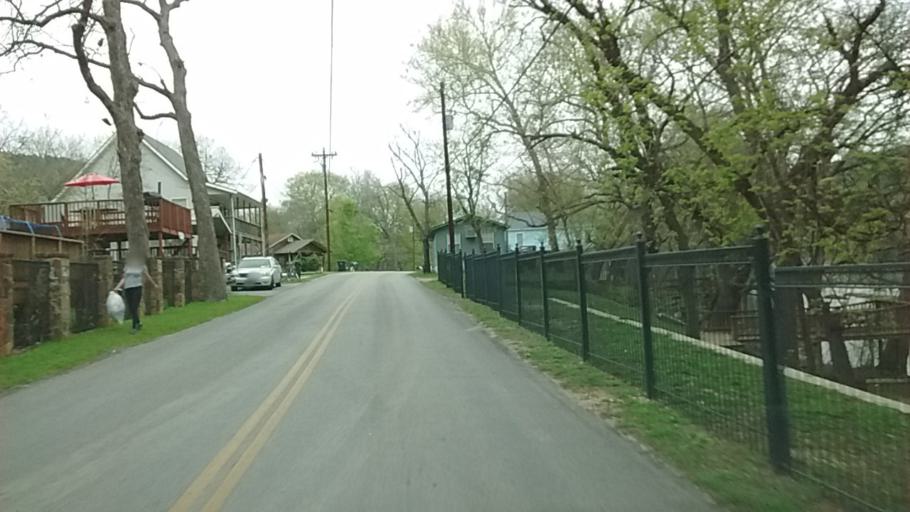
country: US
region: Texas
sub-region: Comal County
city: New Braunfels
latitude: 29.7930
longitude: -98.1518
